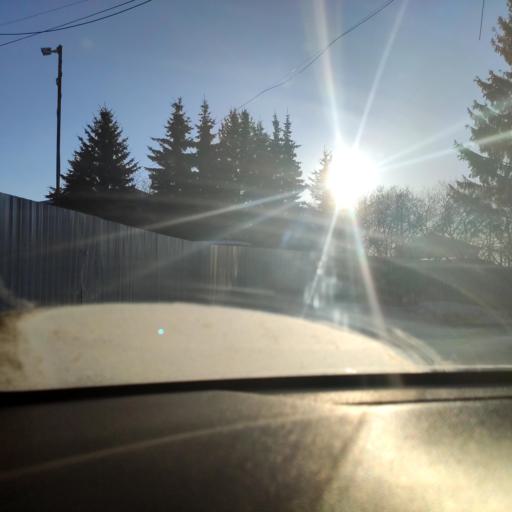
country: RU
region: Tatarstan
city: Staroye Arakchino
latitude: 55.8548
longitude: 49.0175
